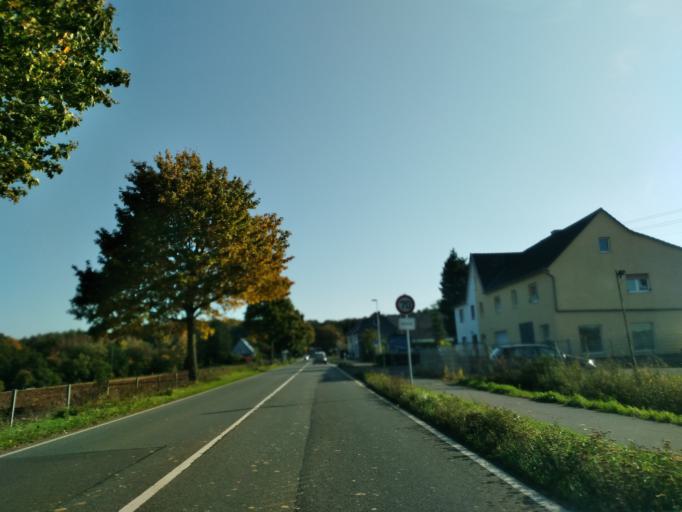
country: DE
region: North Rhine-Westphalia
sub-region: Regierungsbezirk Koln
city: Hennef
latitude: 50.7472
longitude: 7.3441
